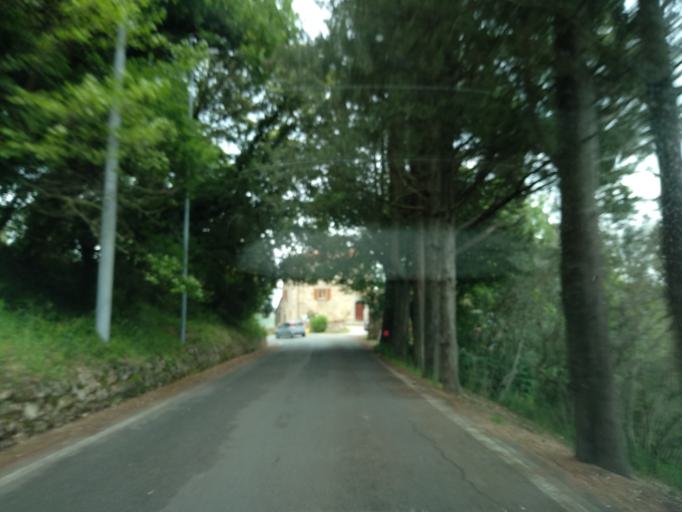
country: IT
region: Tuscany
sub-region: Provincia di Livorno
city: Collesalvetti
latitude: 43.5385
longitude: 10.4445
